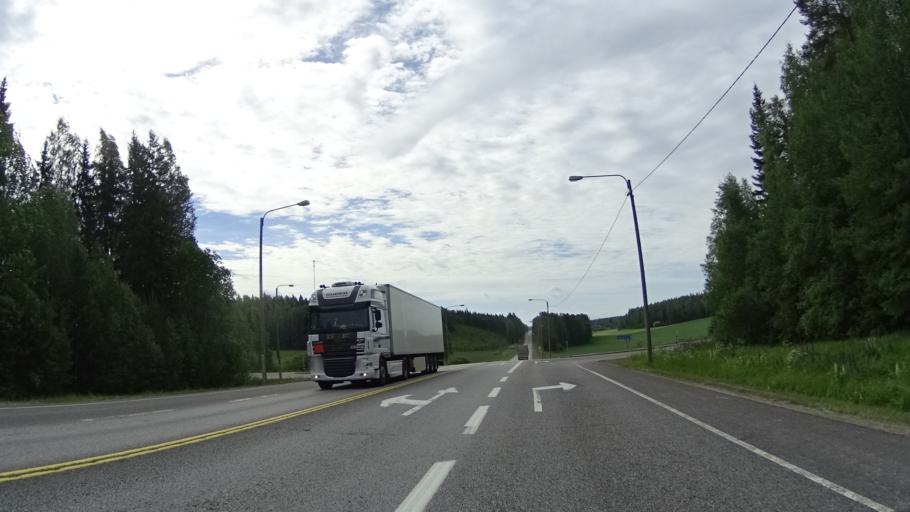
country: FI
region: Uusimaa
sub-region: Helsinki
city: Karkkila
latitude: 60.5081
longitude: 24.2639
